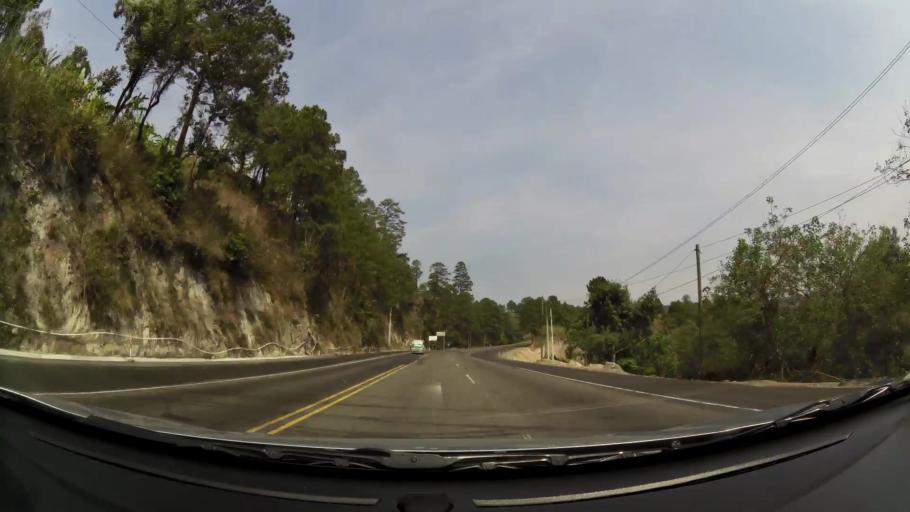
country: HN
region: Comayagua
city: Potrerillos
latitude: 14.5360
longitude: -87.8135
